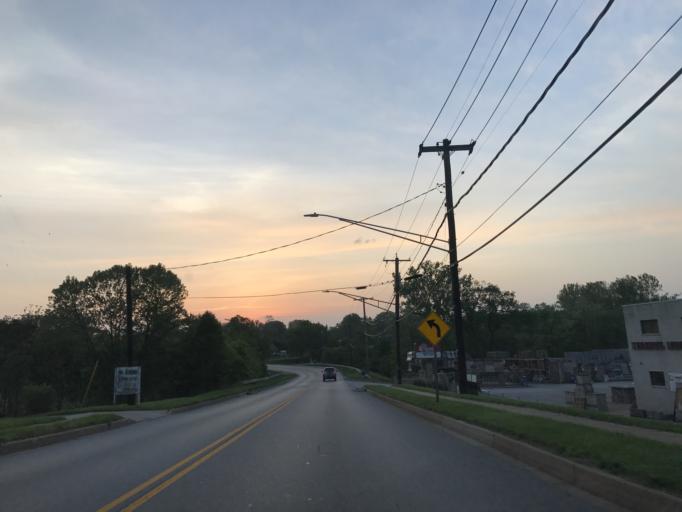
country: US
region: Maryland
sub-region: Anne Arundel County
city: Glen Burnie
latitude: 39.1767
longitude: -76.6198
